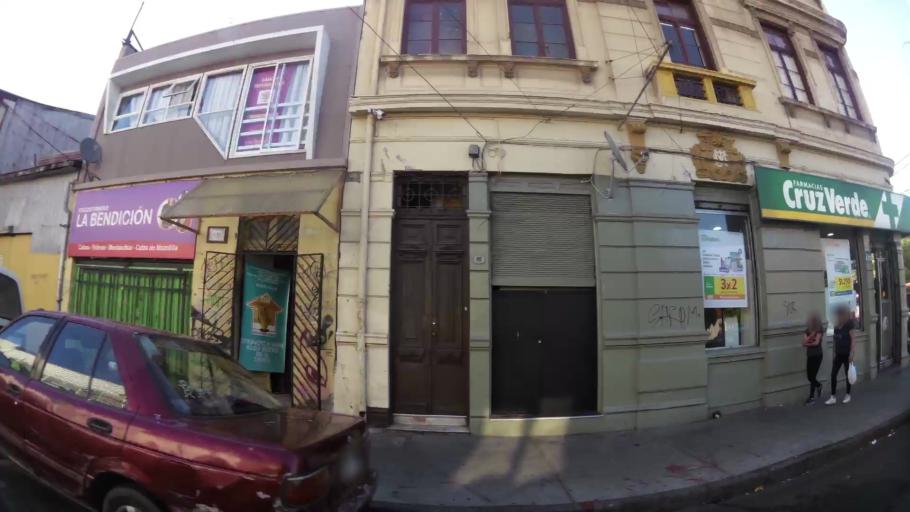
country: CL
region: Valparaiso
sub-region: Provincia de Valparaiso
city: Valparaiso
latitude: -33.0476
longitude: -71.6098
